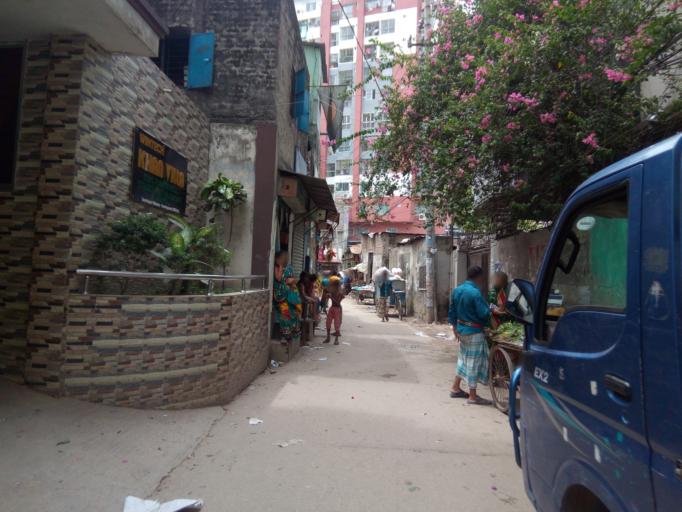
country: BD
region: Dhaka
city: Azimpur
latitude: 23.7494
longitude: 90.3886
